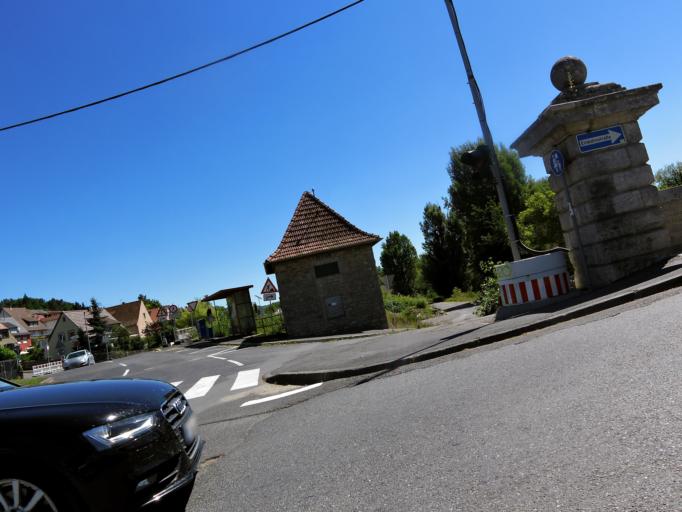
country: DE
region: Bavaria
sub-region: Regierungsbezirk Unterfranken
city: Ochsenfurt
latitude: 49.6684
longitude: 10.0634
